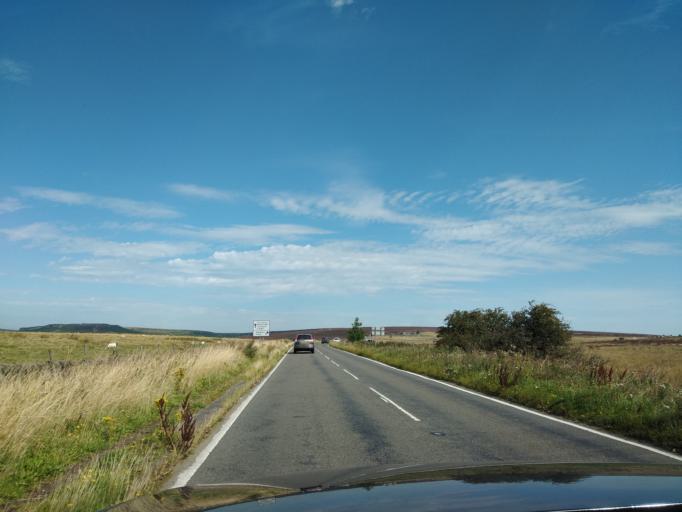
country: GB
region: England
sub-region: Derbyshire
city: Hathersage
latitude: 53.3101
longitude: -1.5991
